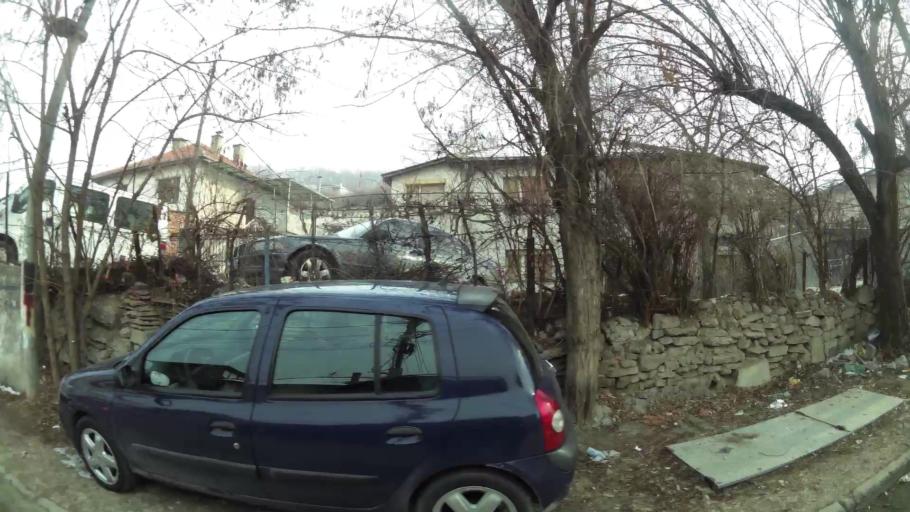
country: MK
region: Cair
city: Cair
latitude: 42.0069
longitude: 21.4468
